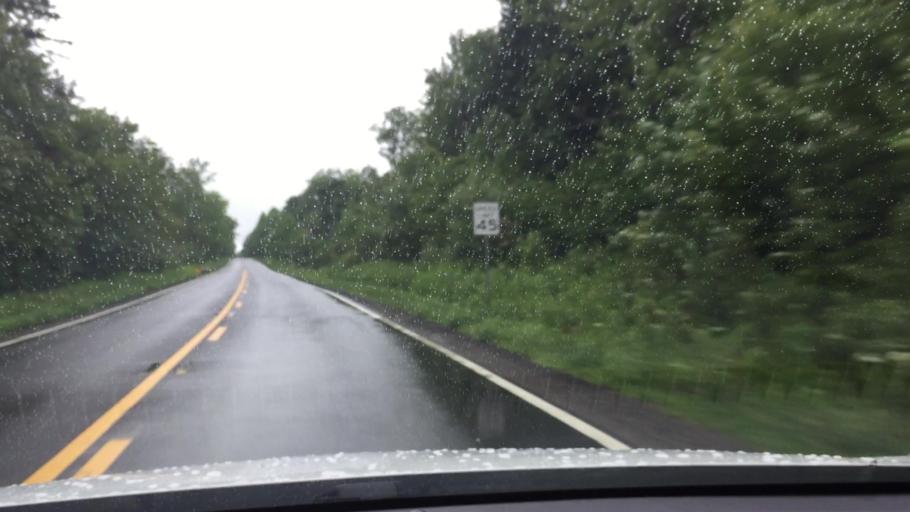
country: US
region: Massachusetts
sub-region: Berkshire County
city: Hinsdale
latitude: 42.3729
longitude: -73.1474
